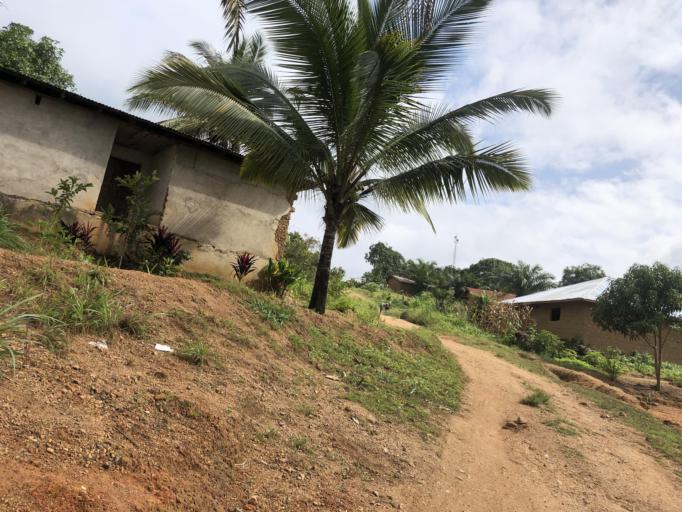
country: SL
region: Eastern Province
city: Kailahun
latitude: 8.2812
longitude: -10.5648
